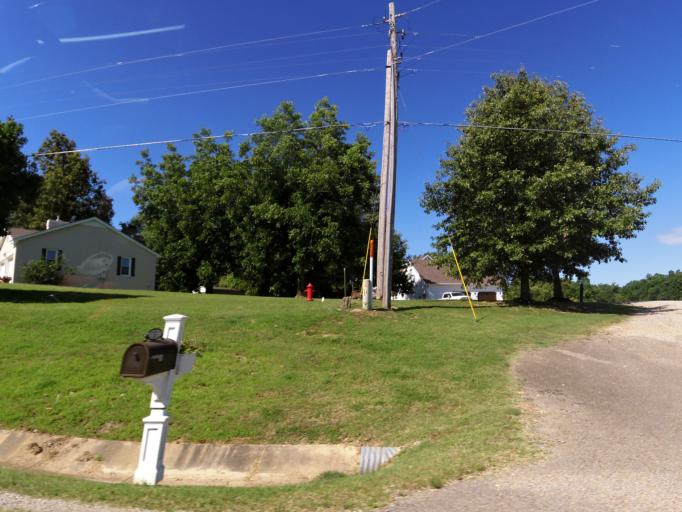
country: US
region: Arkansas
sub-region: Clay County
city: Piggott
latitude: 36.3973
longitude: -90.2061
